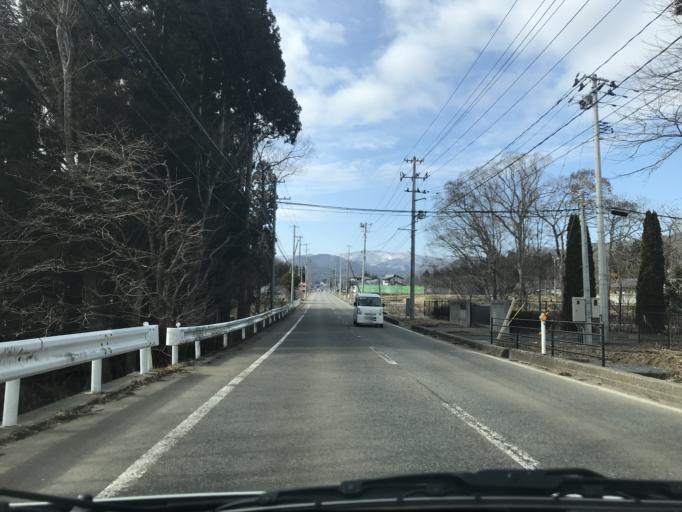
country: JP
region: Iwate
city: Hanamaki
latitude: 39.3998
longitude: 141.0328
